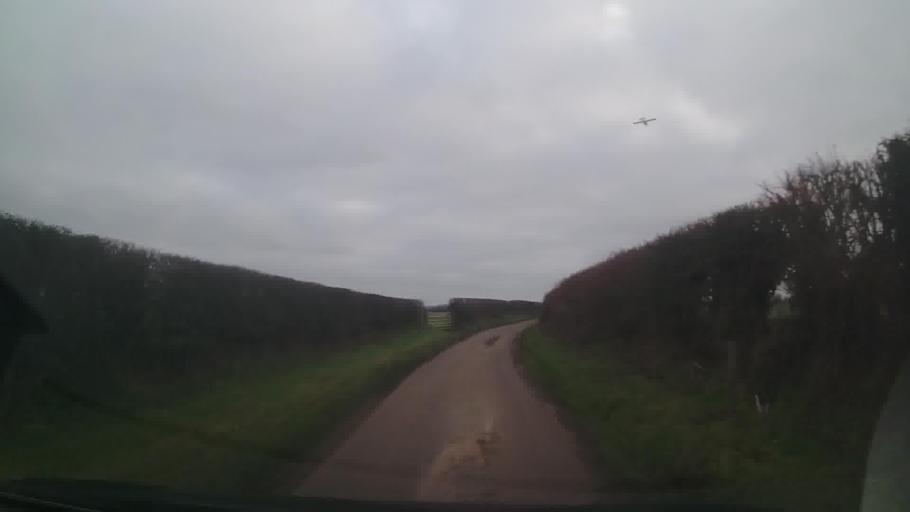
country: GB
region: England
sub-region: Shropshire
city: Wem
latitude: 52.8454
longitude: -2.7719
